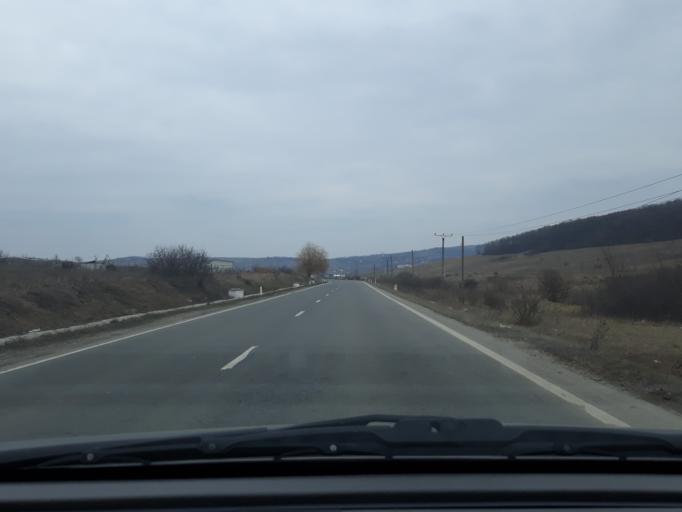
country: RO
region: Salaj
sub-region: Comuna Hereclean
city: Hereclean
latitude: 47.2306
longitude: 22.9738
